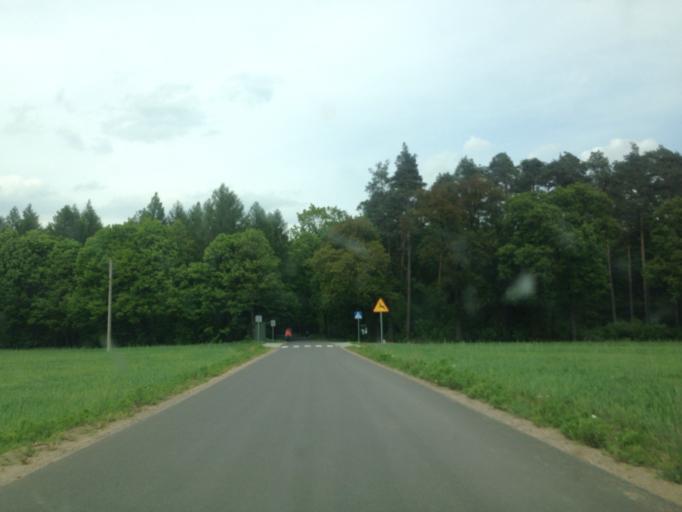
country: PL
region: Kujawsko-Pomorskie
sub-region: Powiat brodnicki
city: Bobrowo
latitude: 53.2658
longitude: 19.3040
